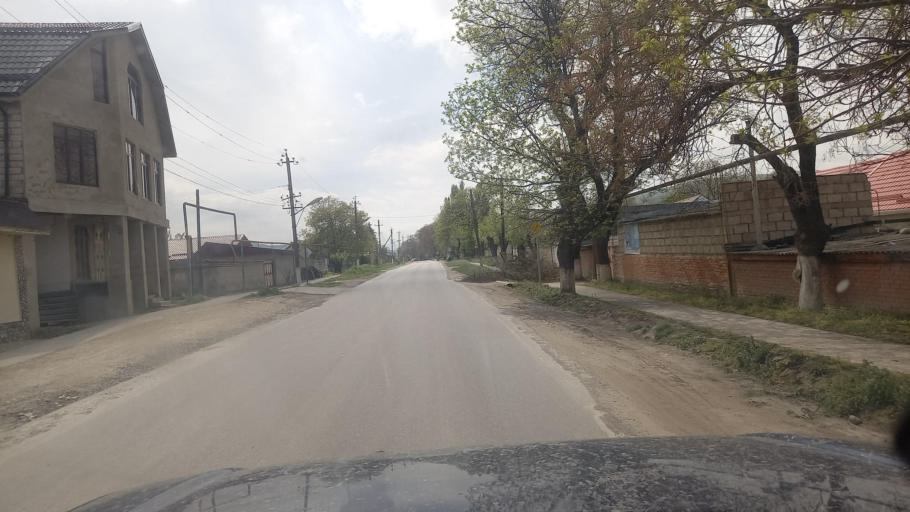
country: RU
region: Kabardino-Balkariya
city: Sarmakovo
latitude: 43.7434
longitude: 43.1972
